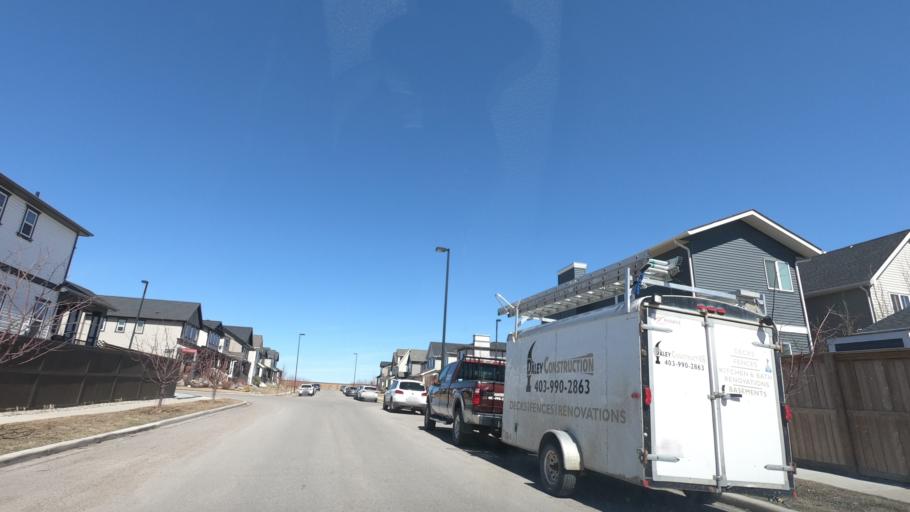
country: CA
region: Alberta
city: Airdrie
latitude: 51.3061
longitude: -114.0451
